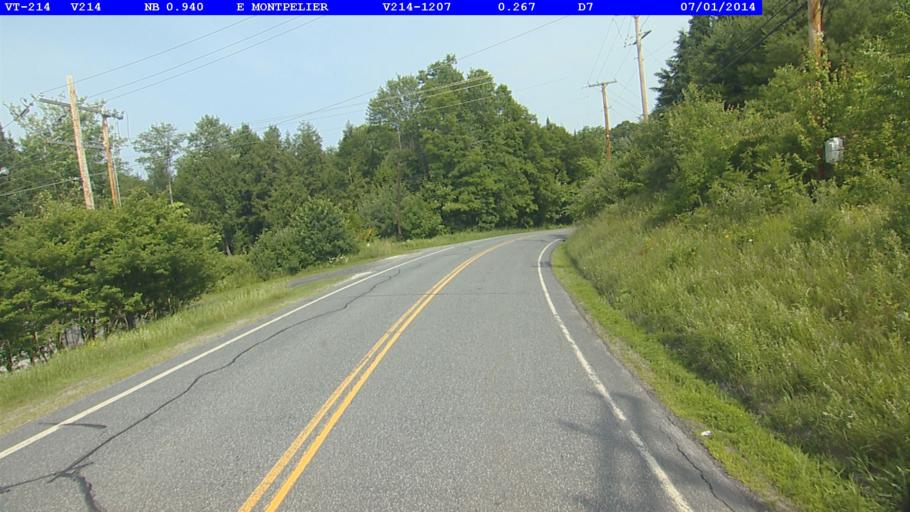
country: US
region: Vermont
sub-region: Washington County
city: Barre
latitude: 44.2893
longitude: -72.4438
